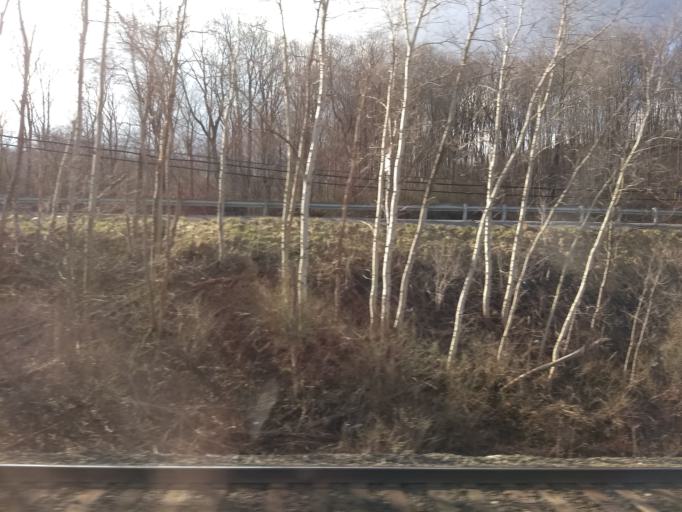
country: US
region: Pennsylvania
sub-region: Cambria County
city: Salix
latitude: 40.3715
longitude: -78.7683
